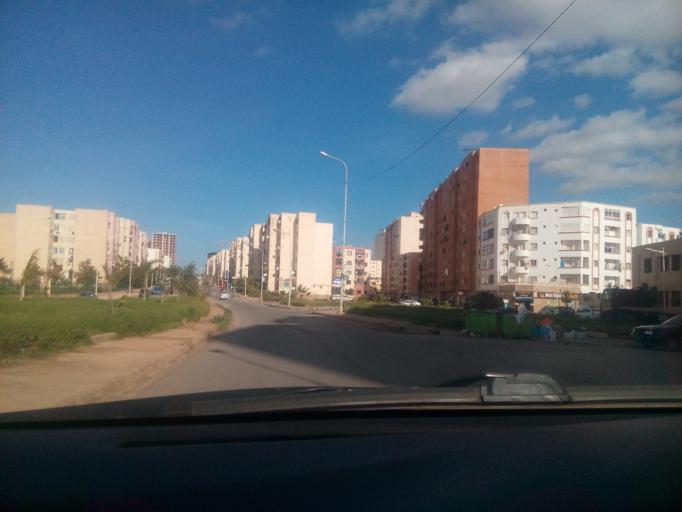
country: DZ
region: Oran
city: Bir el Djir
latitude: 35.7029
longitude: -0.5643
